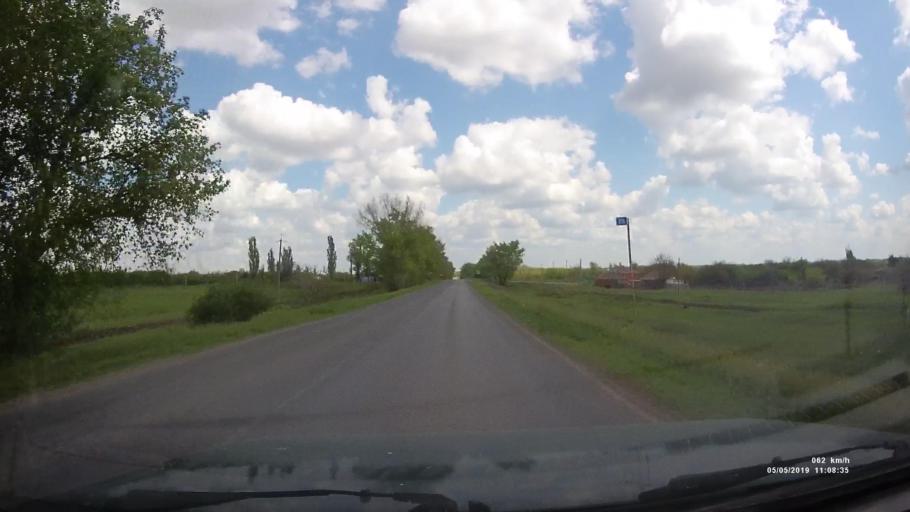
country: RU
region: Rostov
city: Ust'-Donetskiy
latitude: 47.7349
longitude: 40.9154
